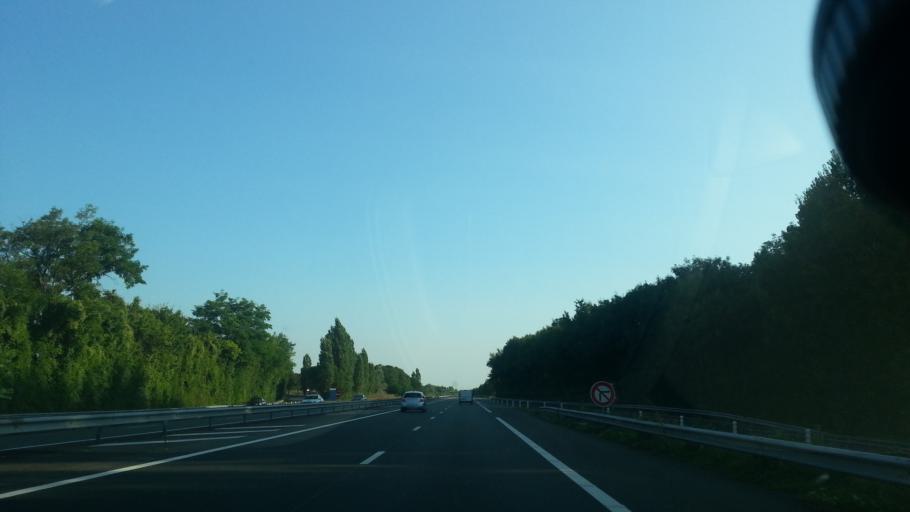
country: FR
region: Poitou-Charentes
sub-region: Departement des Deux-Sevres
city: Beauvoir-sur-Niort
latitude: 46.1144
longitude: -0.5338
